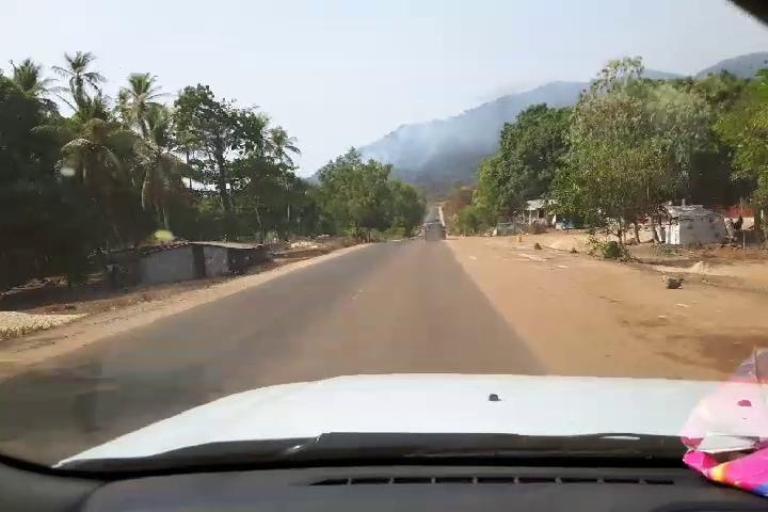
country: SL
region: Western Area
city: Waterloo
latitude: 8.2474
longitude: -13.1526
